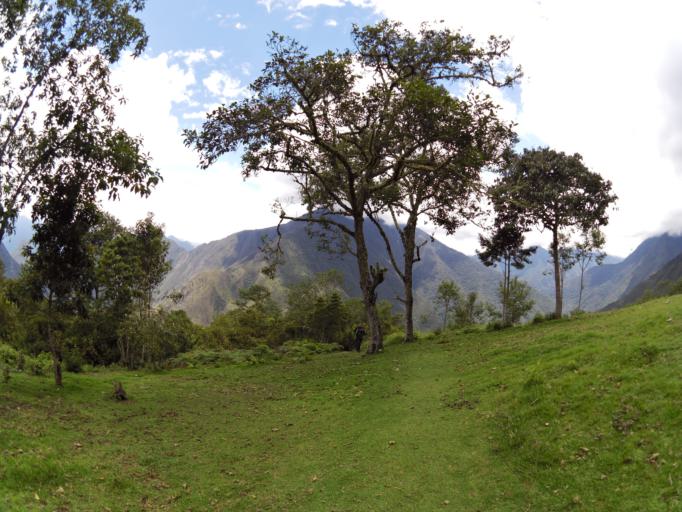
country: PE
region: Cusco
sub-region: Provincia de La Convencion
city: Santa Teresa
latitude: -13.1860
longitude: -72.5812
